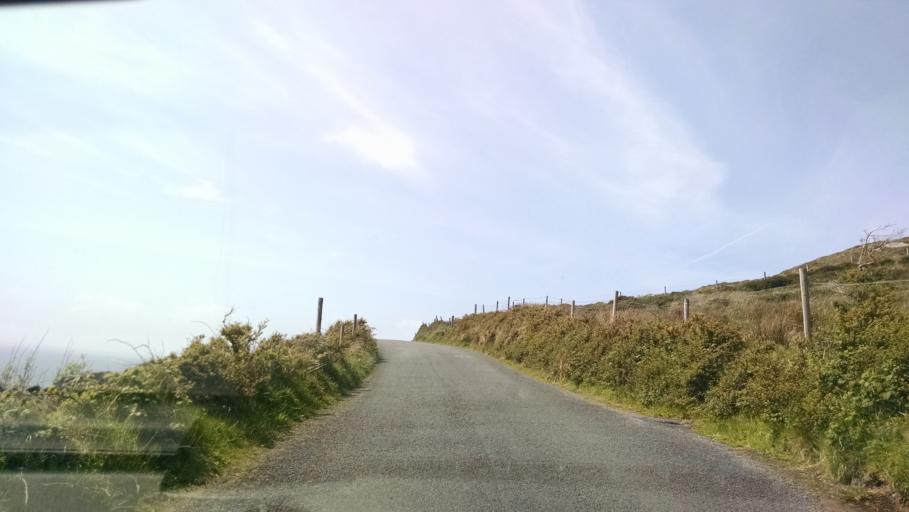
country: IE
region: Connaught
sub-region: County Galway
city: Clifden
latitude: 53.4952
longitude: -10.0743
